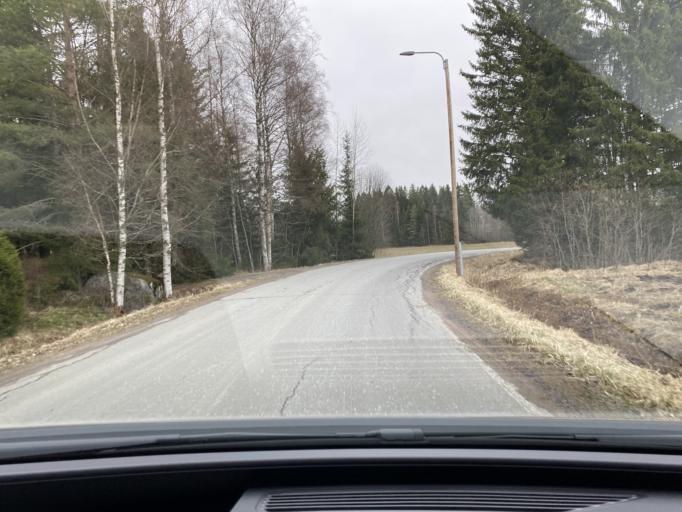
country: FI
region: Satakunta
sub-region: Pori
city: Huittinen
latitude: 61.1683
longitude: 22.7207
